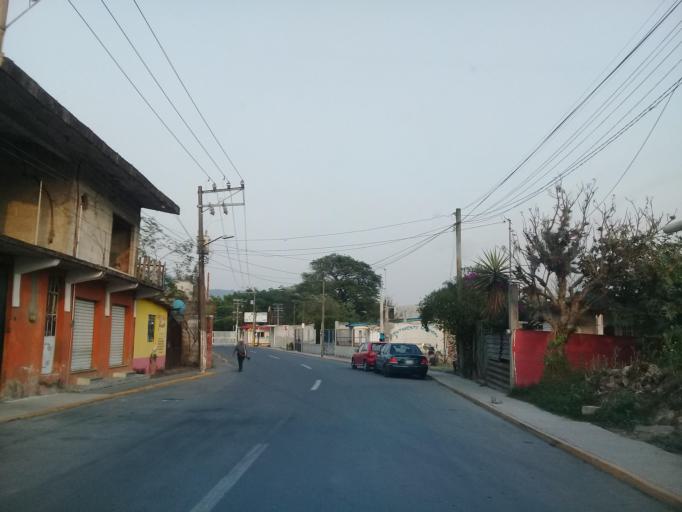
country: MX
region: Veracruz
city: Ixtac Zoquitlan
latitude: 18.8518
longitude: -97.0541
